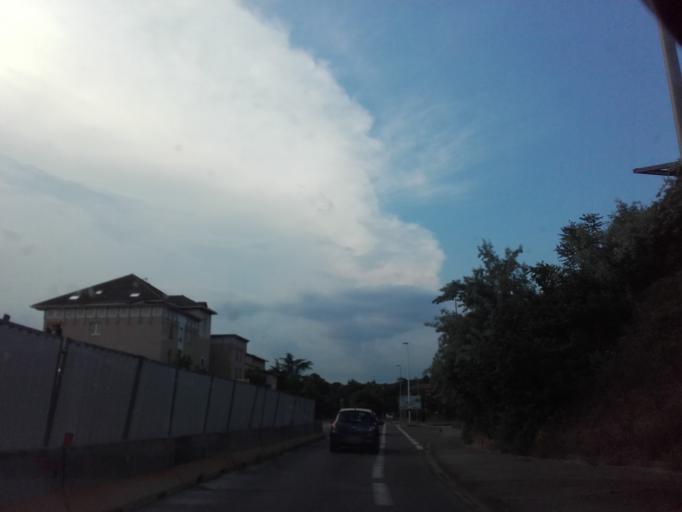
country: FR
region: Rhone-Alpes
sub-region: Departement de l'Isere
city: Le Peage-de-Roussillon
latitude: 45.3756
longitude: 4.7996
